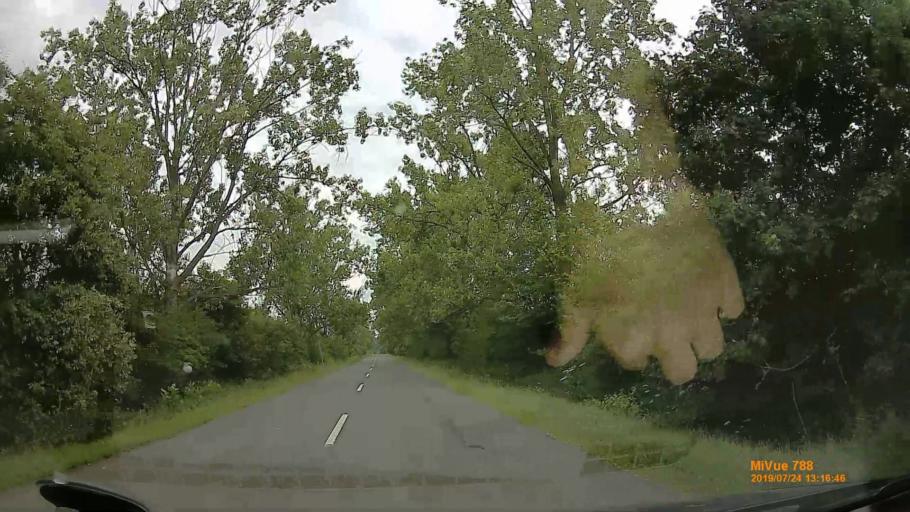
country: HU
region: Szabolcs-Szatmar-Bereg
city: Vasarosnameny
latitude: 48.1974
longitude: 22.3767
